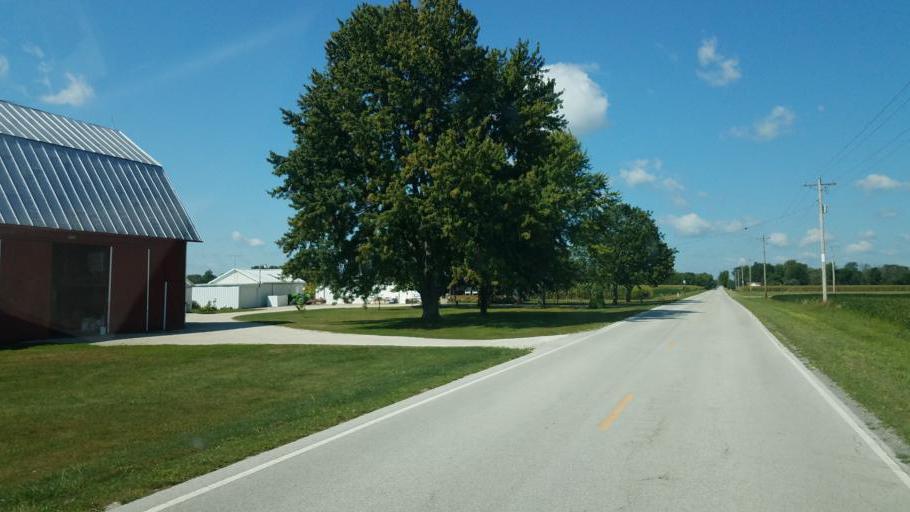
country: US
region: Ohio
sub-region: Wyandot County
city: Carey
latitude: 40.9636
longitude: -83.3223
